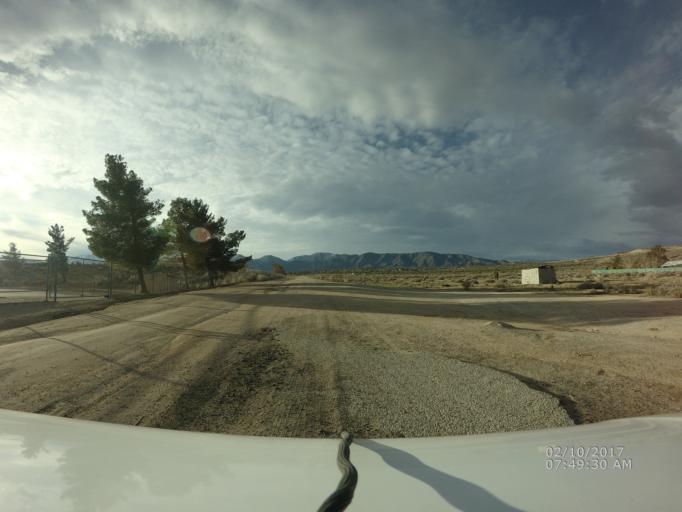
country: US
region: California
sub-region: Los Angeles County
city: Littlerock
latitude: 34.4982
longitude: -117.9011
